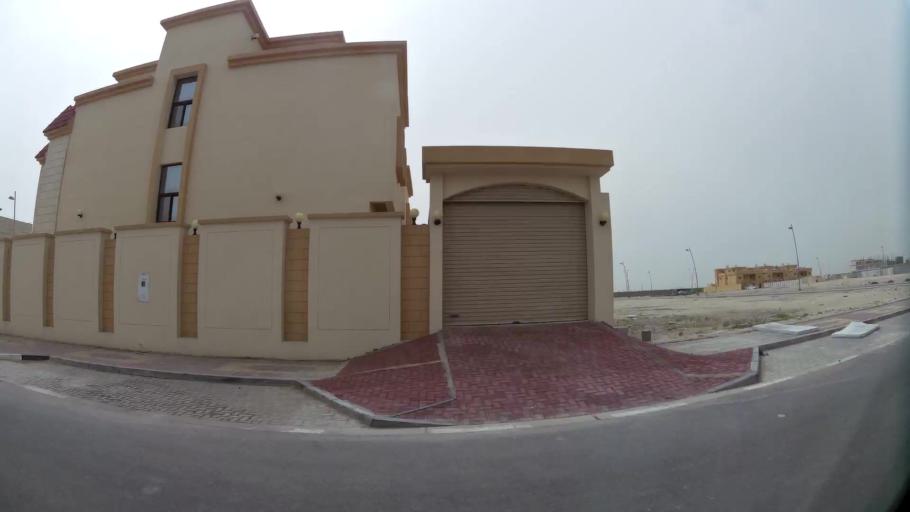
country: QA
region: Baladiyat ad Dawhah
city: Doha
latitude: 25.2338
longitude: 51.5366
